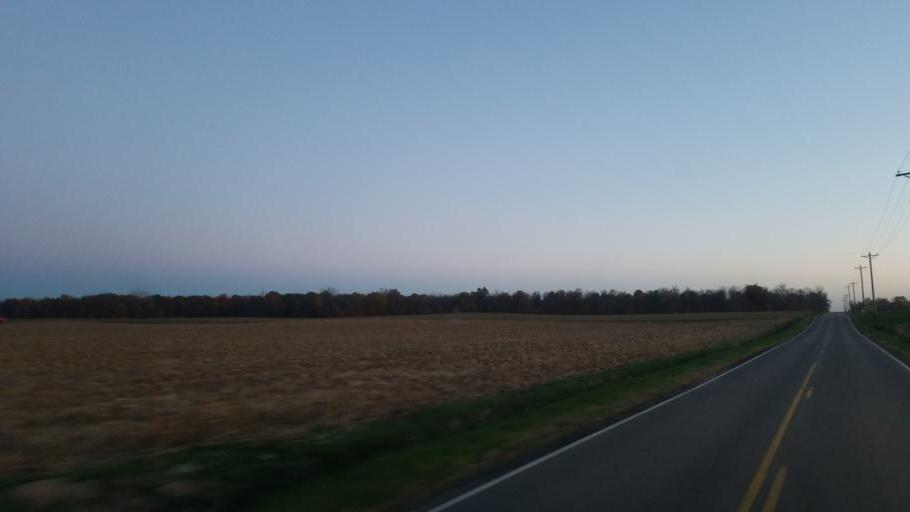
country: US
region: Ohio
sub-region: Richland County
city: Shelby
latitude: 40.9211
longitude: -82.7434
